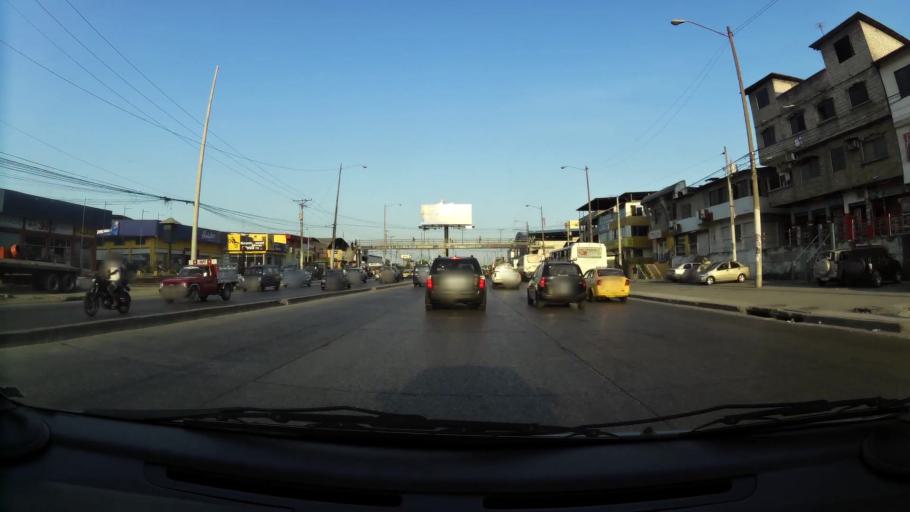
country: EC
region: Guayas
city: Guayaquil
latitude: -2.1414
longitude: -79.9241
